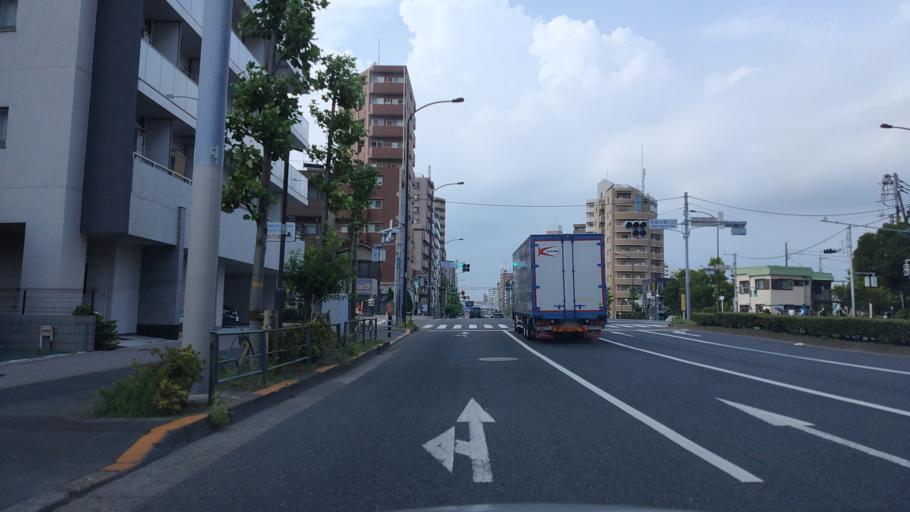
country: JP
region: Tokyo
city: Urayasu
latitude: 35.6553
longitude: 139.8725
